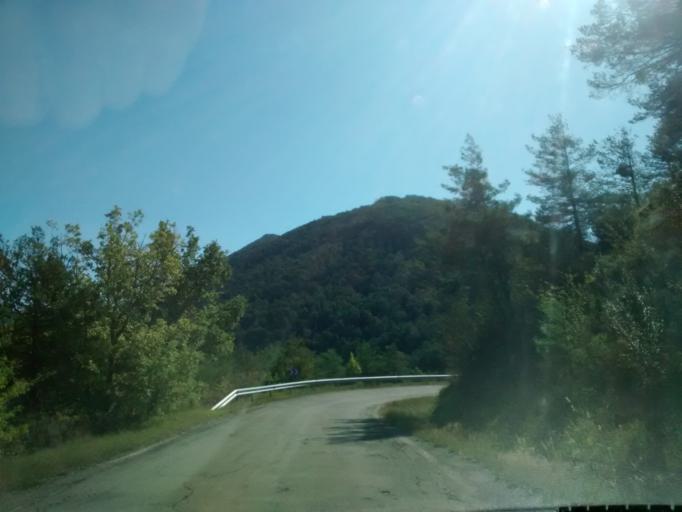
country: ES
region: Aragon
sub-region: Provincia de Huesca
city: Jaca
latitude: 42.4897
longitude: -0.5641
